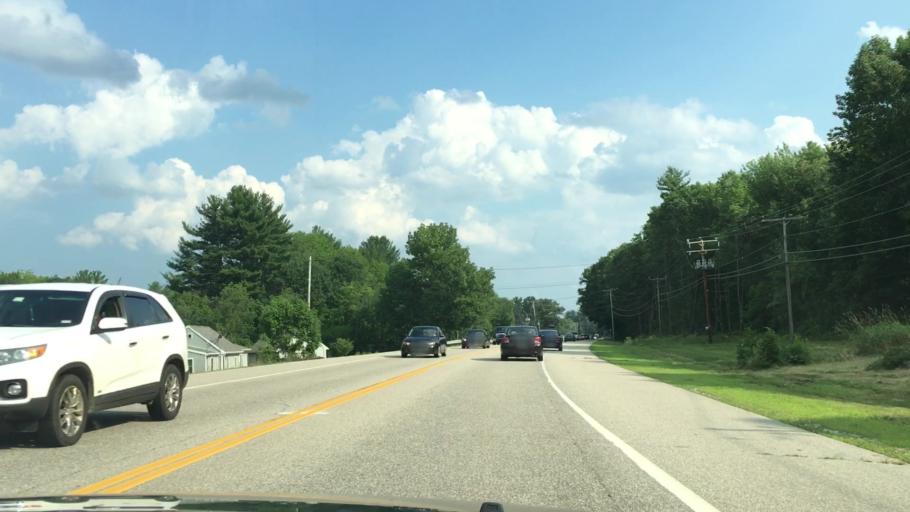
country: US
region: New Hampshire
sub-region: Strafford County
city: Farmington
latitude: 43.3539
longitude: -71.0278
